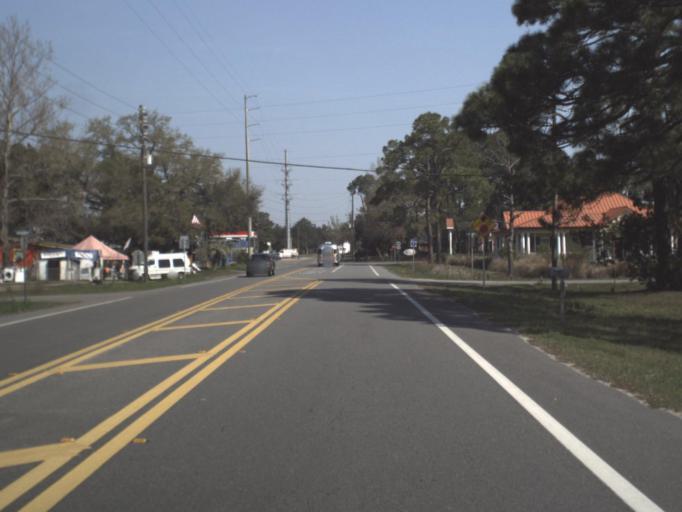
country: US
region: Florida
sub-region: Franklin County
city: Eastpoint
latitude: 29.7347
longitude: -84.8879
